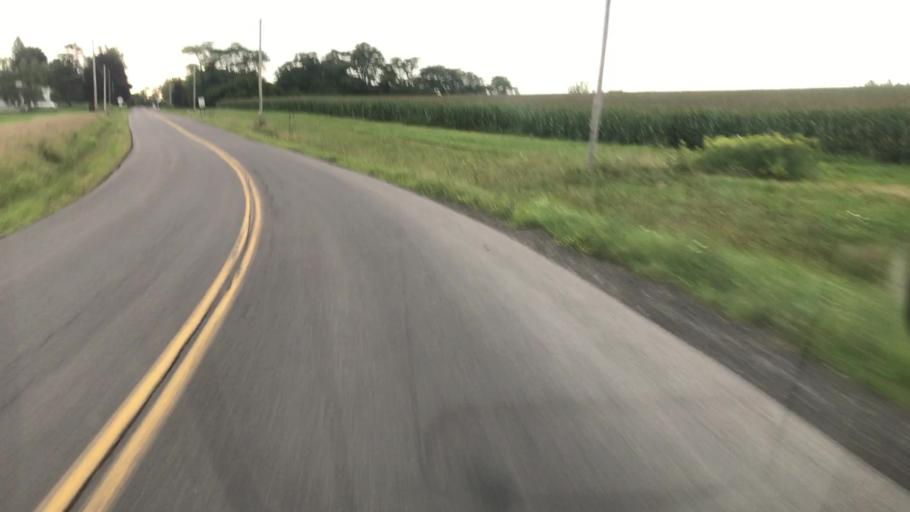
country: US
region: New York
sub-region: Cayuga County
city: Melrose Park
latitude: 42.9200
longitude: -76.5269
